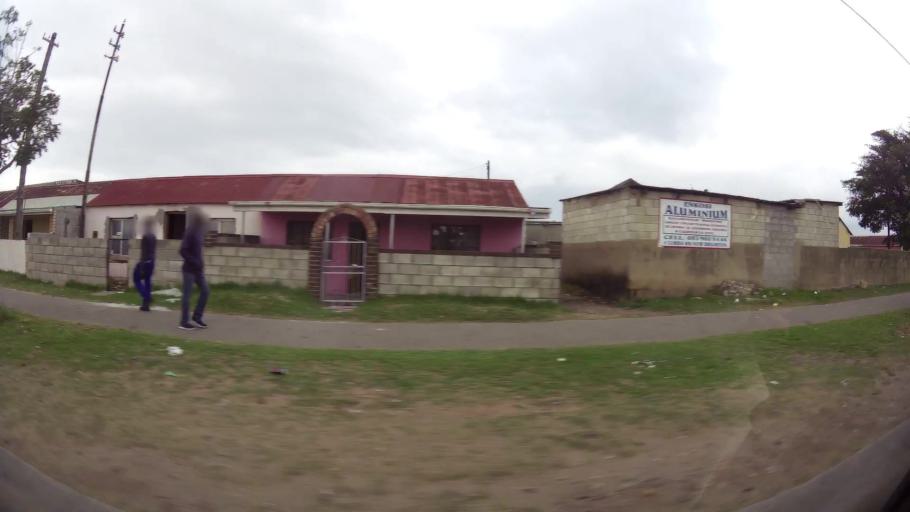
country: ZA
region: Eastern Cape
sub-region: Nelson Mandela Bay Metropolitan Municipality
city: Port Elizabeth
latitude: -33.9022
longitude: 25.5991
